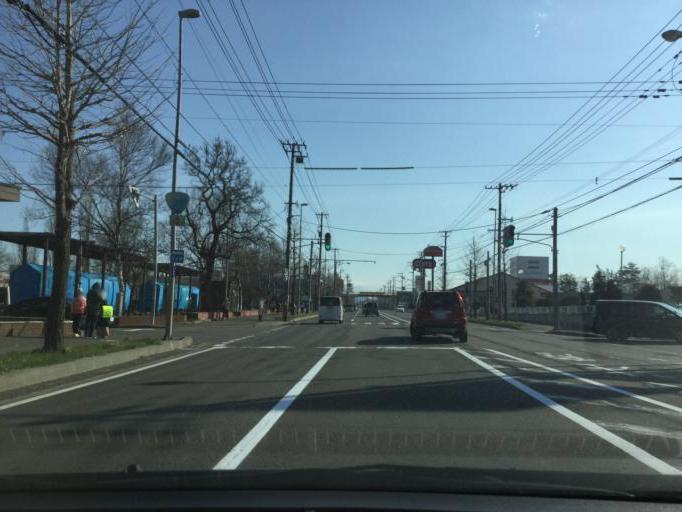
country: JP
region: Hokkaido
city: Iwamizawa
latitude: 43.1982
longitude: 141.7728
